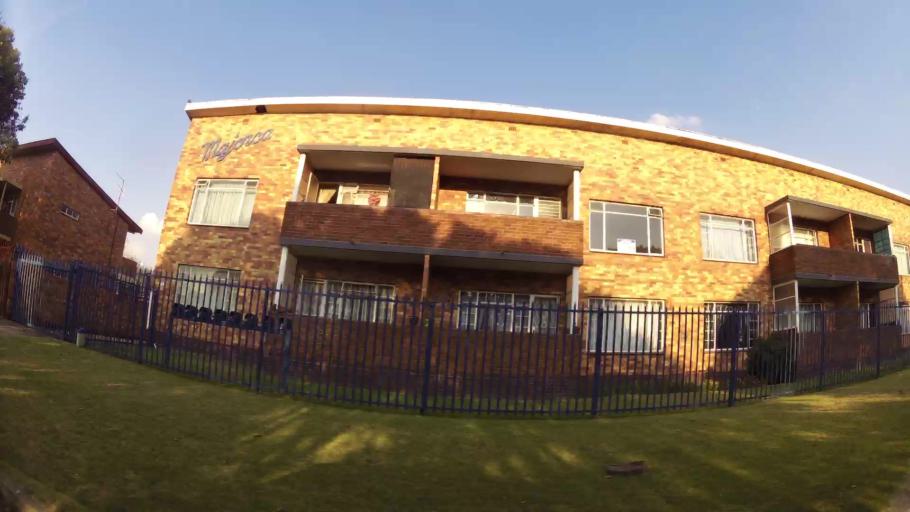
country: ZA
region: Gauteng
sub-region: Ekurhuleni Metropolitan Municipality
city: Springs
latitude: -26.2917
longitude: 28.4435
